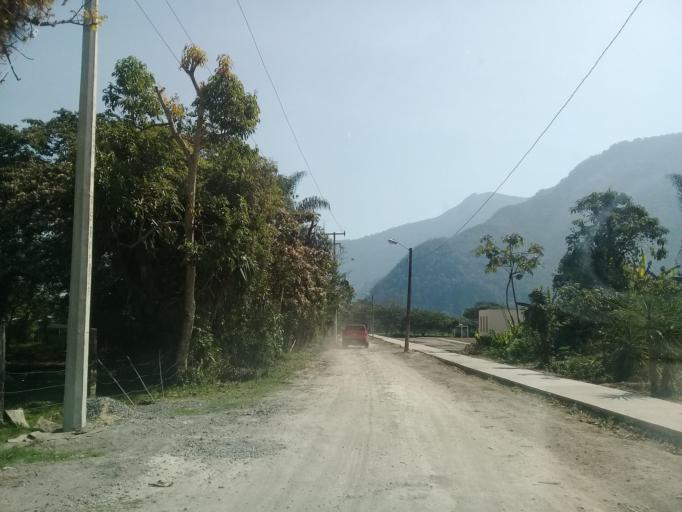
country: MX
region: Veracruz
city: Rafael Delgado
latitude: 18.7939
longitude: -97.0077
